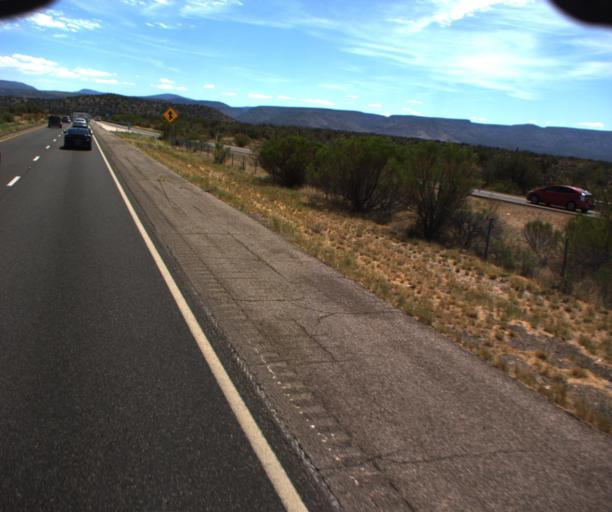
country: US
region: Arizona
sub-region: Yavapai County
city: Lake Montezuma
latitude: 34.6736
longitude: -111.7704
